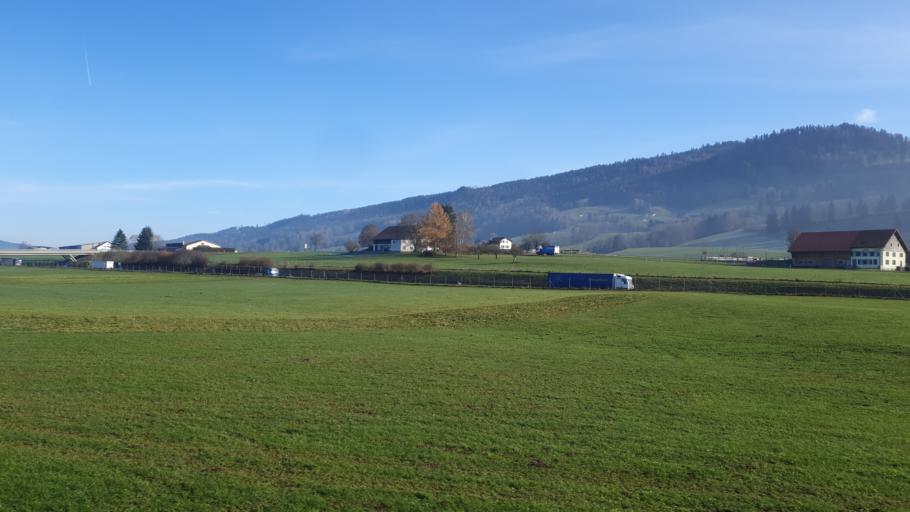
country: CH
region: Fribourg
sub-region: Veveyse District
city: Chatel-Saint-Denis
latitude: 46.5837
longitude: 6.9252
